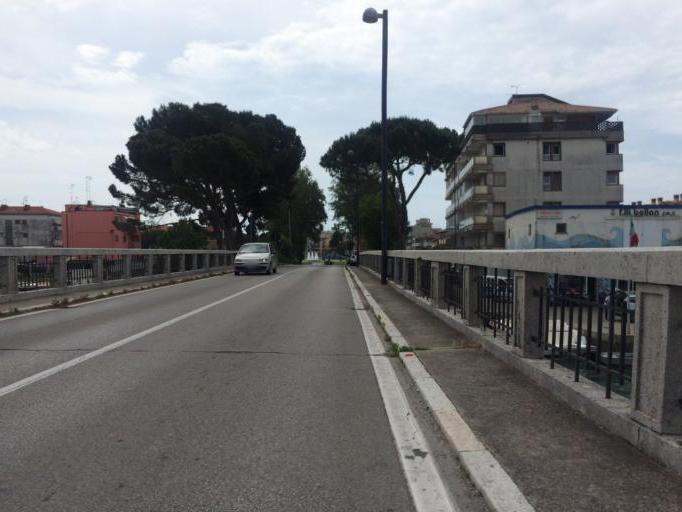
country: IT
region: Friuli Venezia Giulia
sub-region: Provincia di Gorizia
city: Grado
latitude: 45.6831
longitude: 13.3864
